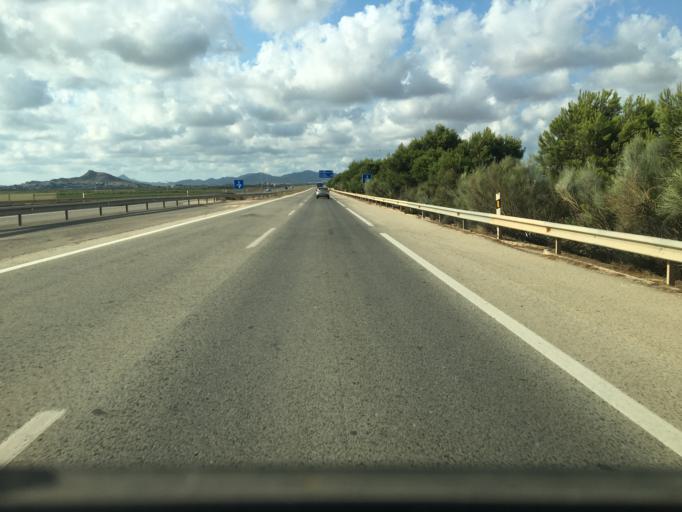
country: ES
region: Murcia
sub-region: Murcia
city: Los Alcazares
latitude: 37.7135
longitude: -0.8684
